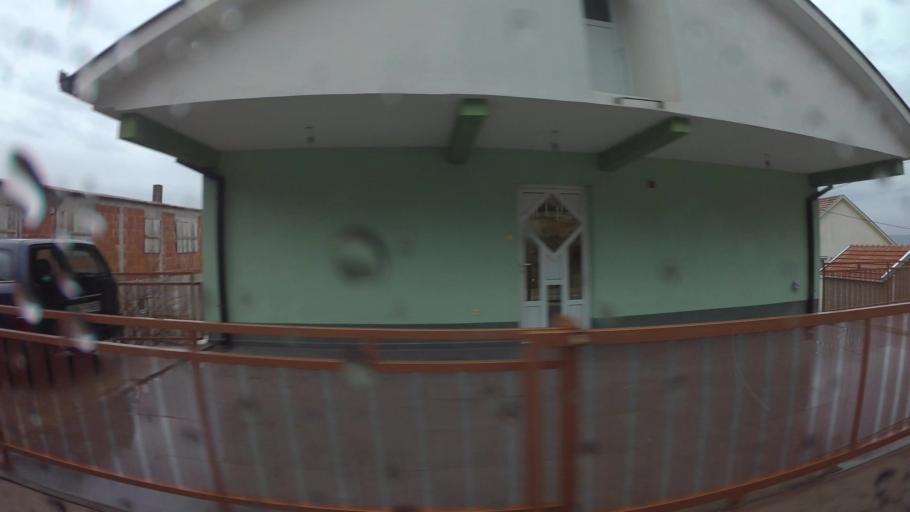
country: BA
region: Federation of Bosnia and Herzegovina
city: Rodoc
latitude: 43.3026
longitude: 17.8534
